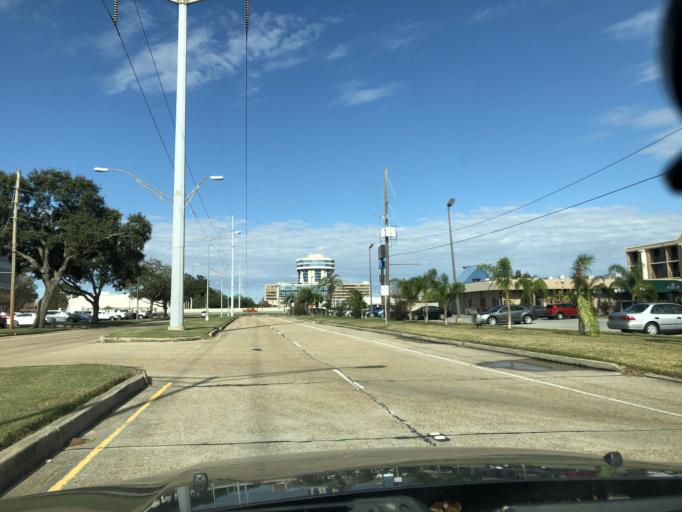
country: US
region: Louisiana
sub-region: Jefferson Parish
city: Metairie
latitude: 29.9955
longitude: -90.1597
